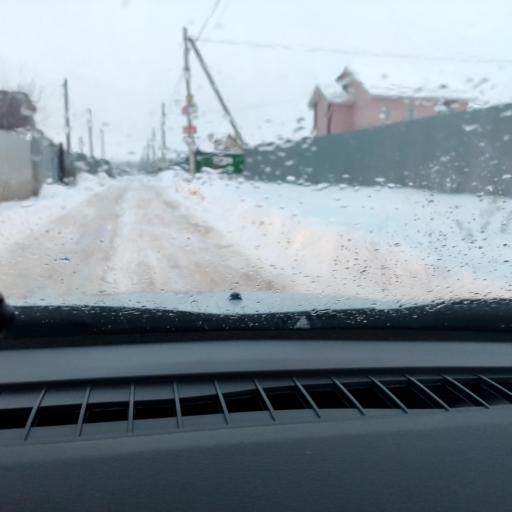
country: RU
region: Samara
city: Dubovyy Umet
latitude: 53.0310
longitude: 50.2265
